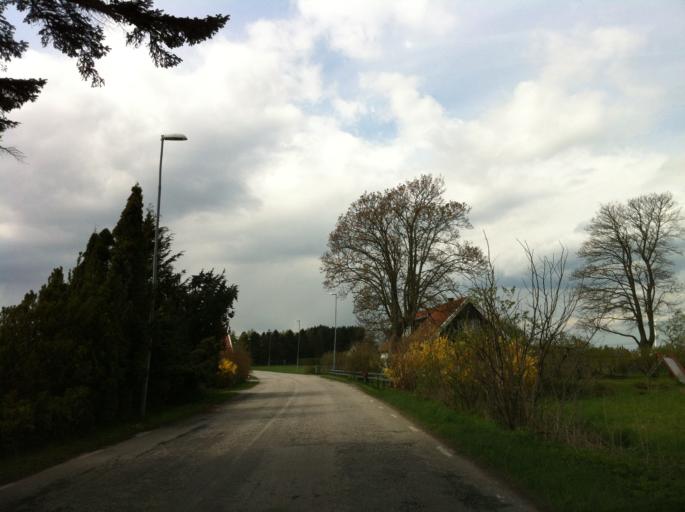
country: SE
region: Skane
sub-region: Kavlinge Kommun
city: Kaevlinge
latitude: 55.8108
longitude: 13.1438
